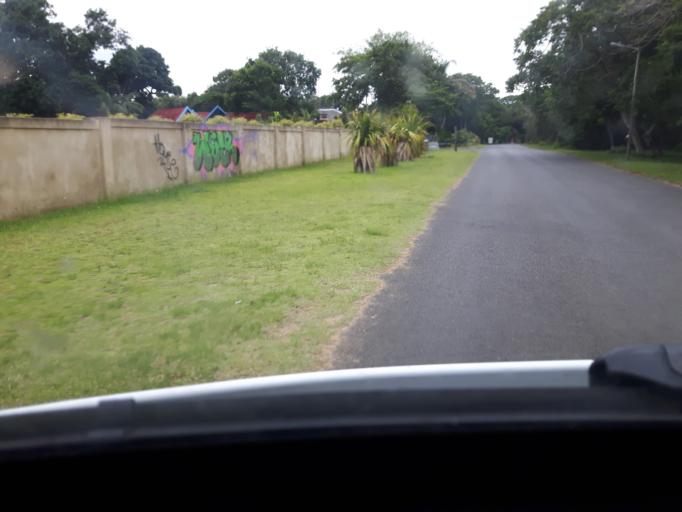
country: ZA
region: KwaZulu-Natal
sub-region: uMkhanyakude District Municipality
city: Mtubatuba
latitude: -28.3804
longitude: 32.4101
